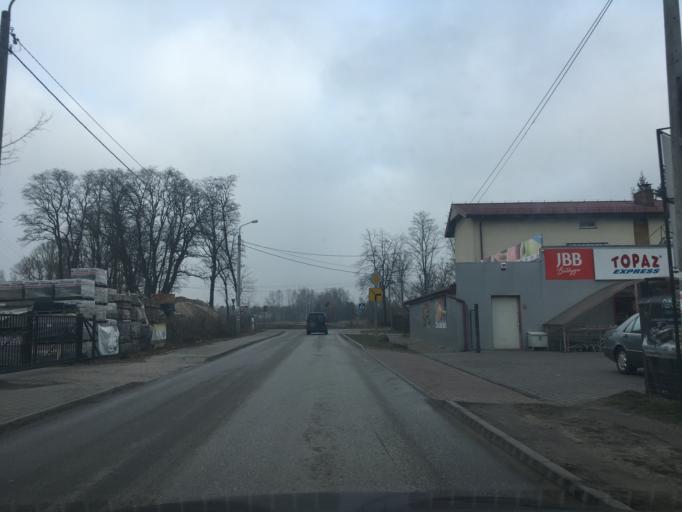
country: PL
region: Masovian Voivodeship
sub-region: Powiat piaseczynski
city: Lesznowola
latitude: 52.0389
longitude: 20.9446
